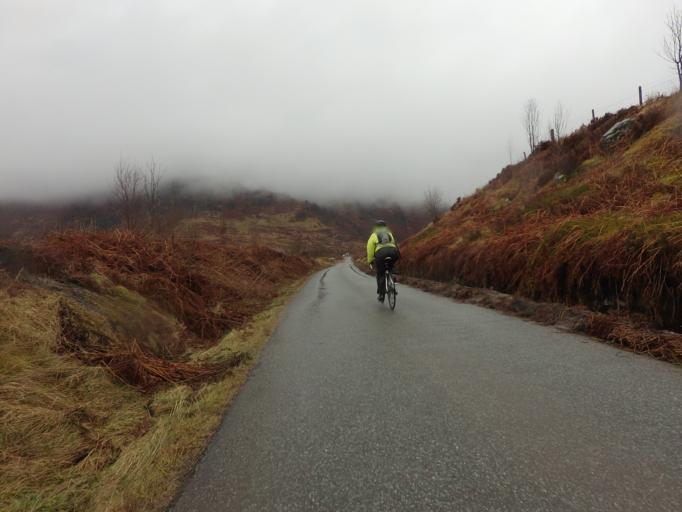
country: GB
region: Scotland
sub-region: West Dunbartonshire
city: Balloch
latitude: 56.2506
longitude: -4.5879
